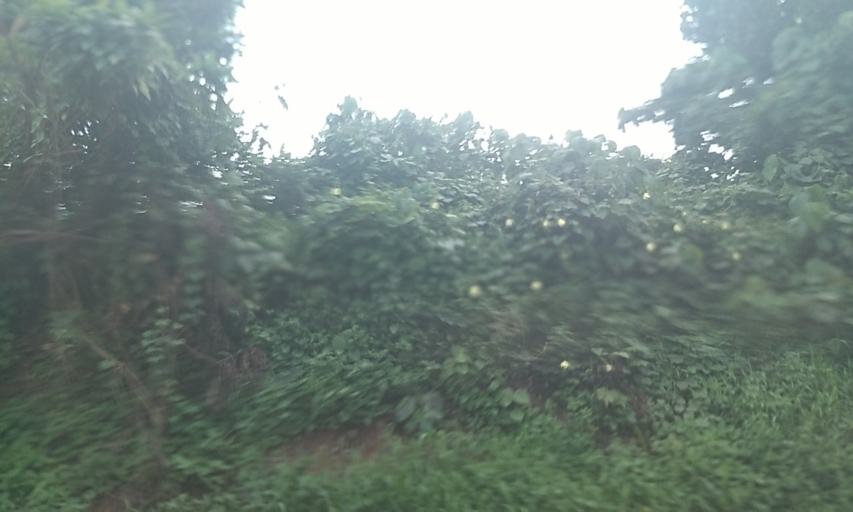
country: UG
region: Central Region
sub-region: Wakiso District
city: Wakiso
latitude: 0.3571
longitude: 32.4549
